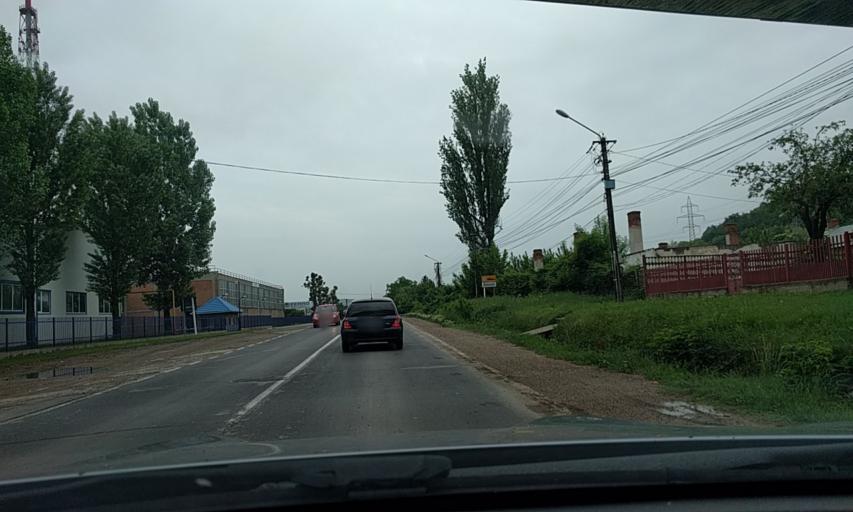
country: RO
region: Dambovita
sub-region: Comuna Aninoasa
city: Sateni
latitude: 44.9851
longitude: 25.4169
